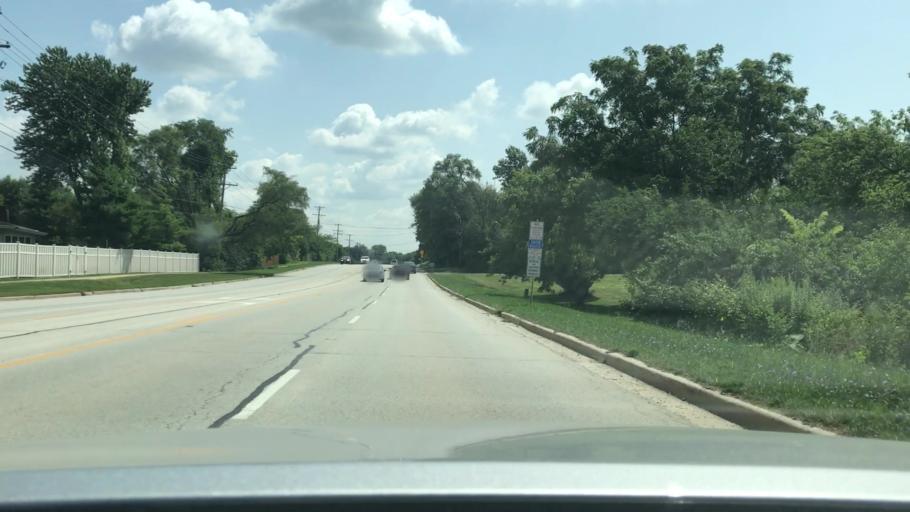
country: US
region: Illinois
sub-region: DuPage County
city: Woodridge
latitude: 41.7291
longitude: -88.0194
